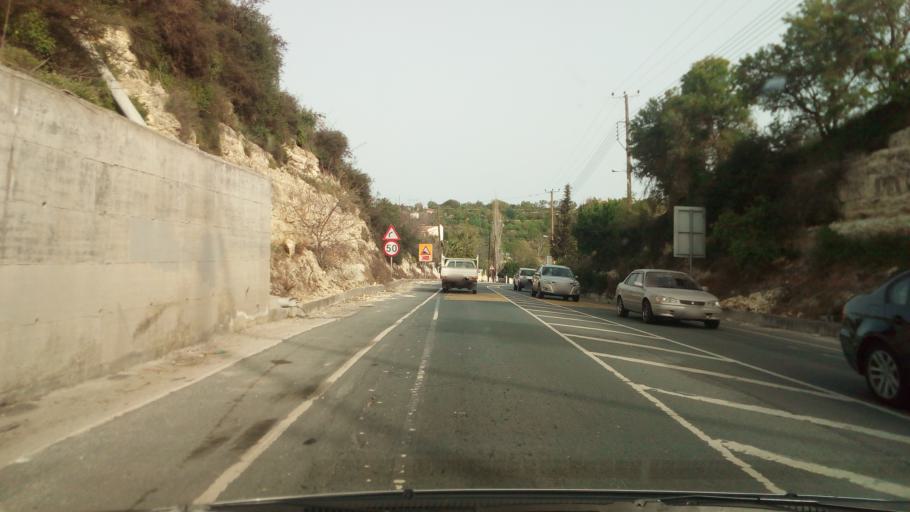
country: CY
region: Pafos
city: Mesogi
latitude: 34.8425
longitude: 32.4674
